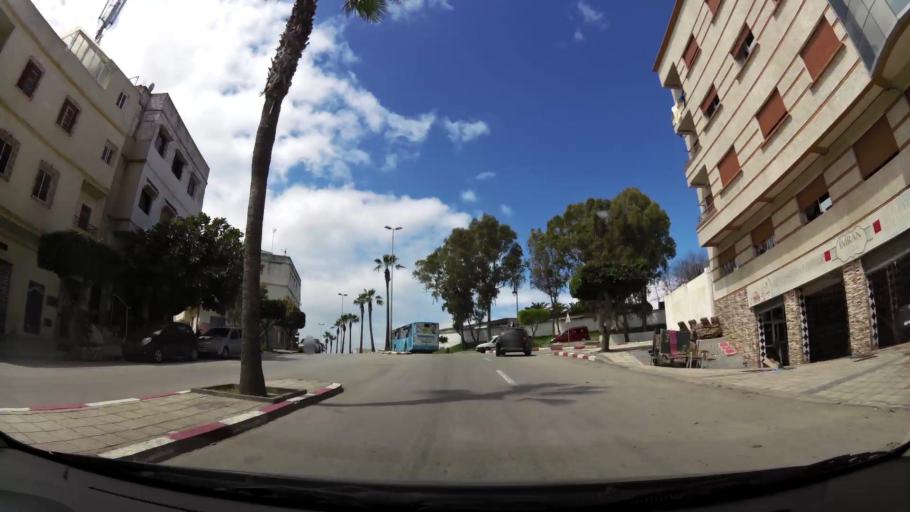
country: MA
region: Tanger-Tetouan
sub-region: Tanger-Assilah
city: Tangier
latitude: 35.7668
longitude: -5.8294
